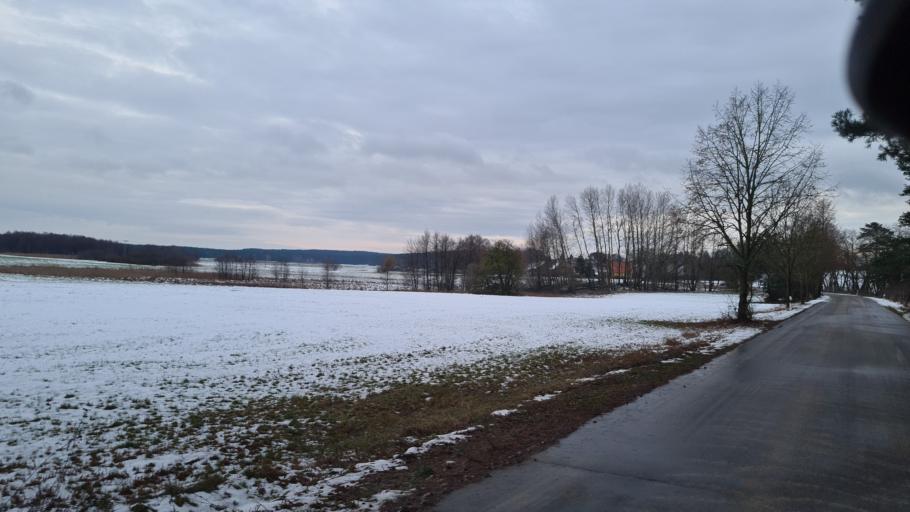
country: DE
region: Brandenburg
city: Schenkendobern
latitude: 51.9144
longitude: 14.5735
